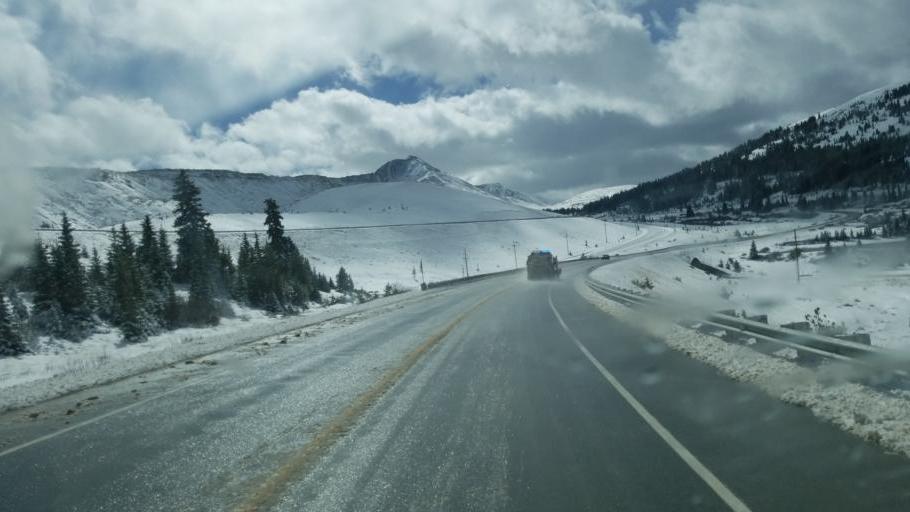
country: US
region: Colorado
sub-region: Lake County
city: Leadville
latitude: 39.3833
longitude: -106.1906
